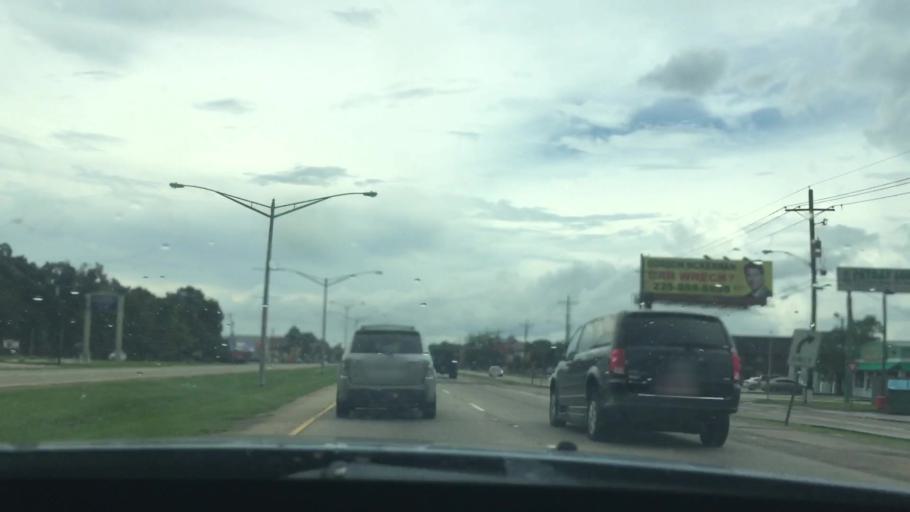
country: US
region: Louisiana
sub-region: East Baton Rouge Parish
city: Monticello
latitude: 30.4569
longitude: -91.0704
